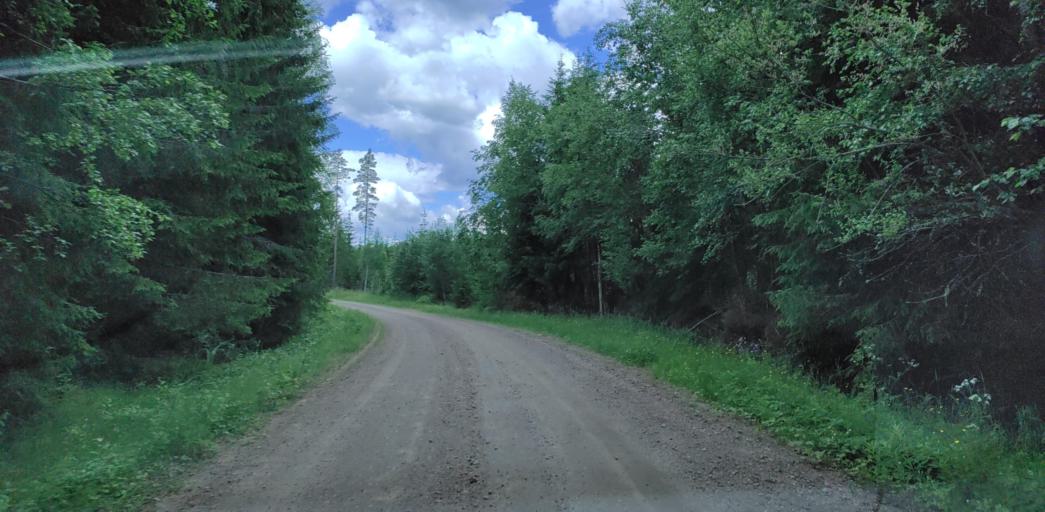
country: SE
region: Vaermland
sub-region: Hagfors Kommun
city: Ekshaerad
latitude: 60.0873
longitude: 13.4367
